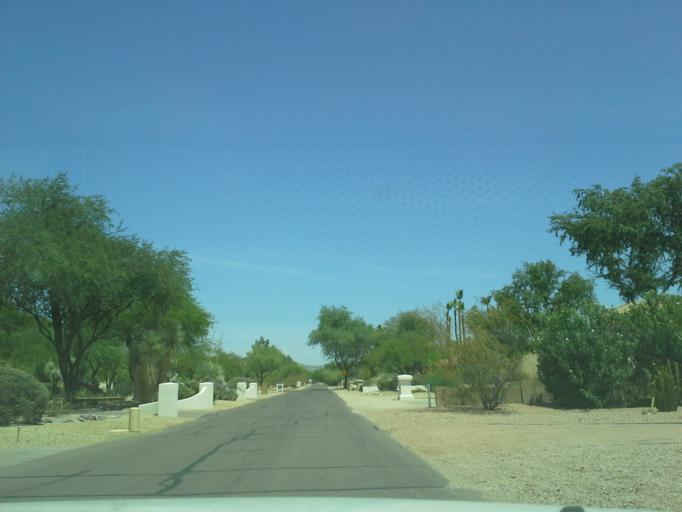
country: US
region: Arizona
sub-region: Maricopa County
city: Scottsdale
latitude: 33.5897
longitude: -111.8645
